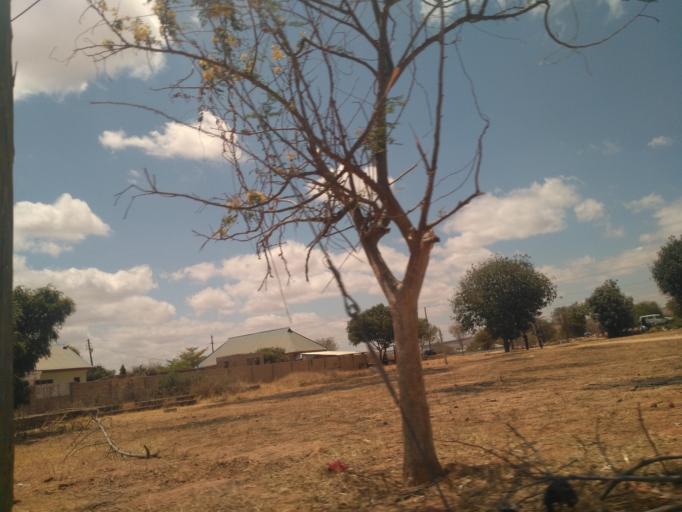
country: TZ
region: Dodoma
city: Kisasa
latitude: -6.1668
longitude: 35.7801
